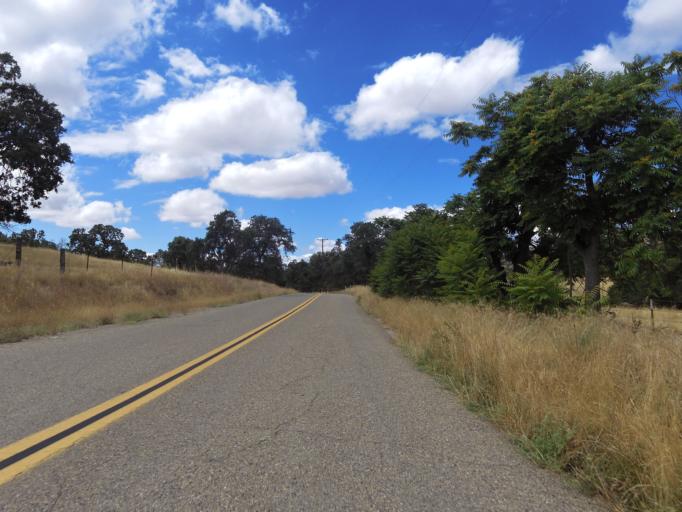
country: US
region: California
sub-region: Madera County
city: Yosemite Lakes
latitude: 37.2263
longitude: -119.8710
